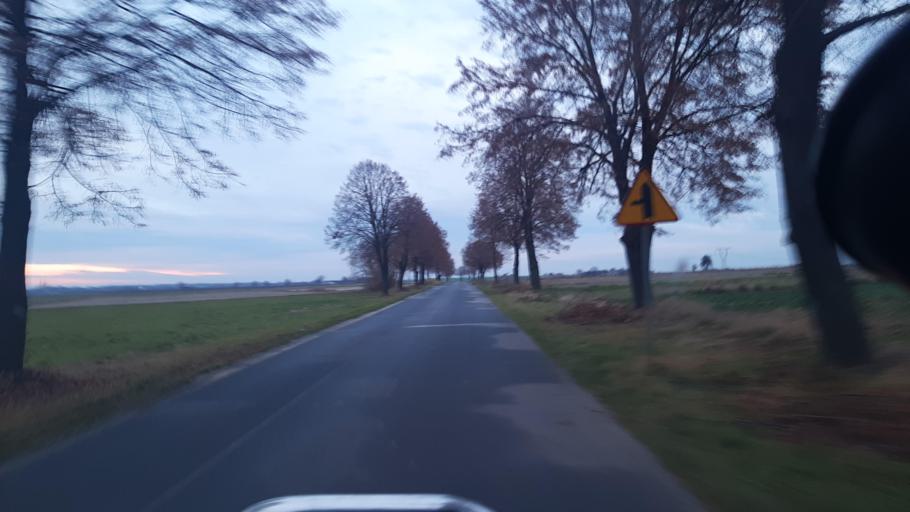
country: PL
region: Lublin Voivodeship
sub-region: Powiat lubelski
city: Garbow
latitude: 51.3777
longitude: 22.3714
